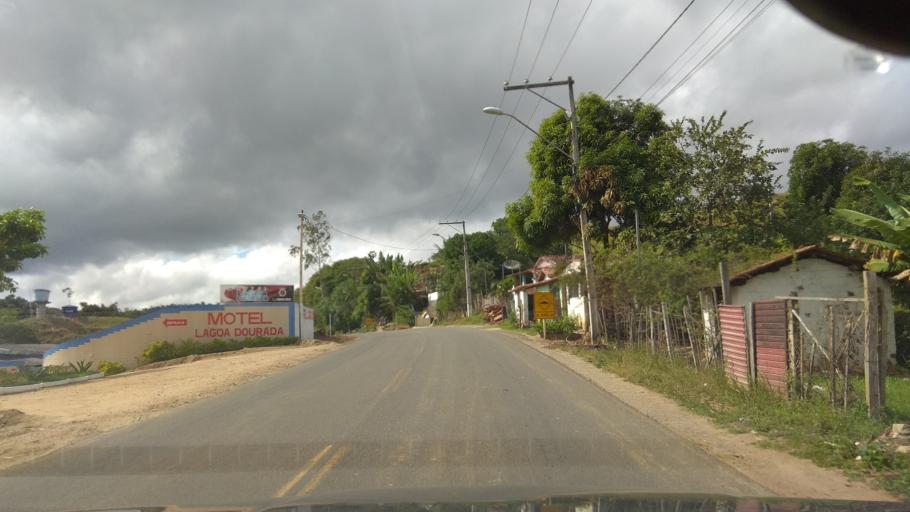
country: BR
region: Bahia
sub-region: Ubaira
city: Ubaira
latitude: -13.2546
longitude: -39.5866
